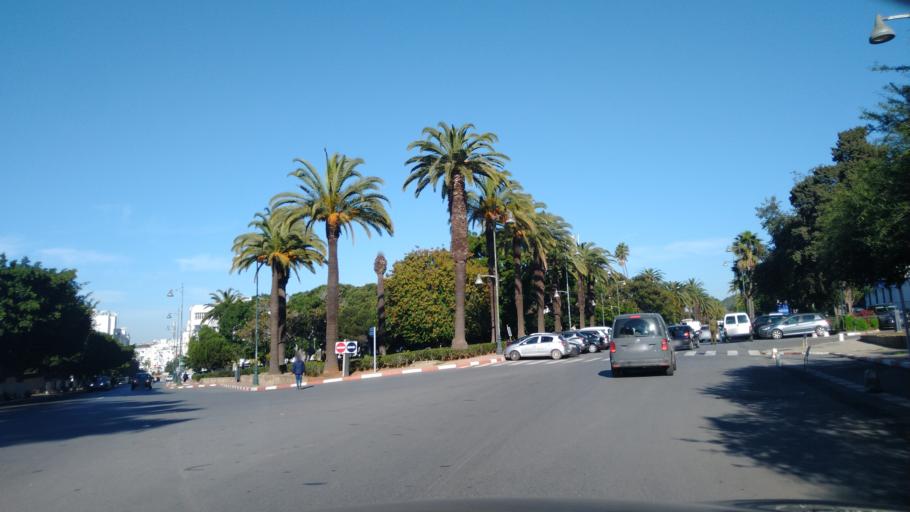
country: MA
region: Rabat-Sale-Zemmour-Zaer
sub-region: Rabat
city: Rabat
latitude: 34.0094
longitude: -6.8289
